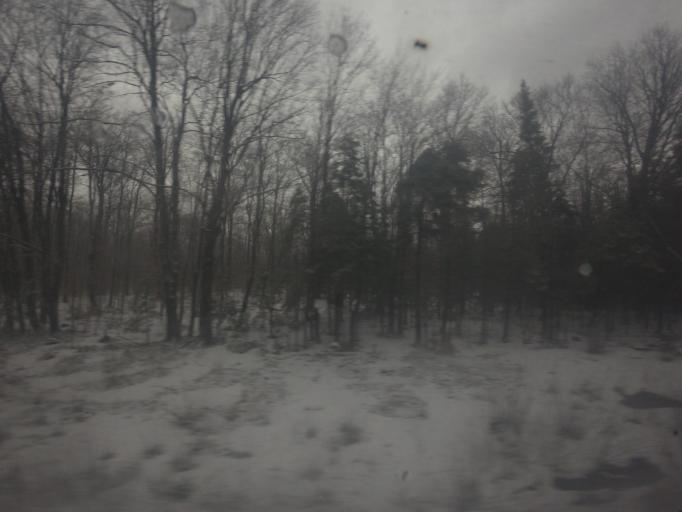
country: CA
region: Ontario
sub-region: Lanark County
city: Smiths Falls
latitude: 44.9823
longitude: -75.9810
